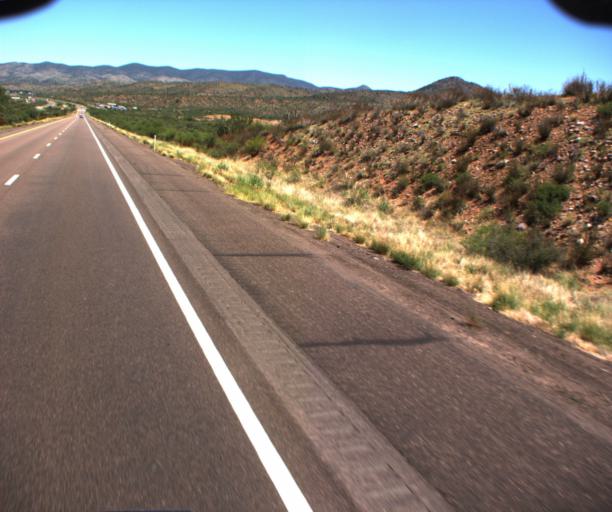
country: US
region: Arizona
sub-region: Gila County
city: Payson
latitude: 34.0771
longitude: -111.3567
